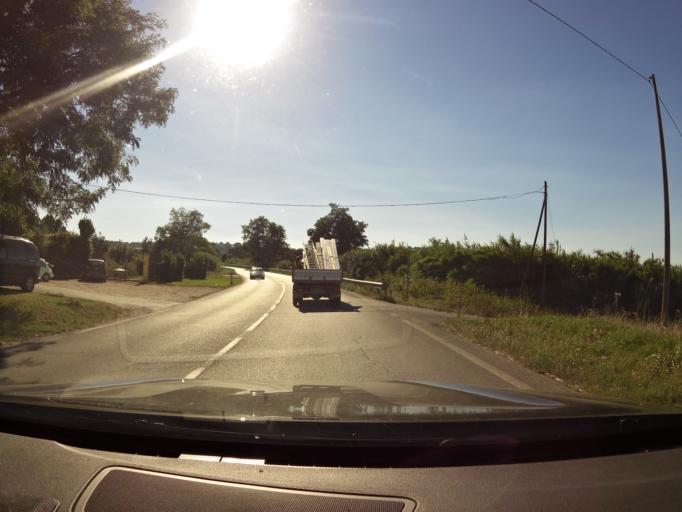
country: IT
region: The Marches
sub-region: Provincia di Ancona
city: Villa Musone
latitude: 43.4771
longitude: 13.5867
